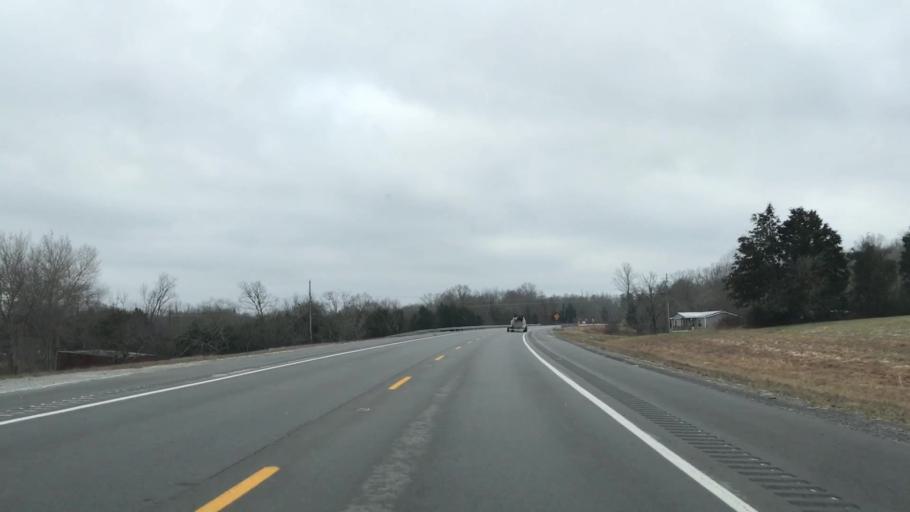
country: US
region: Kentucky
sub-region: Adair County
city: Columbia
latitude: 37.0532
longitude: -85.3612
